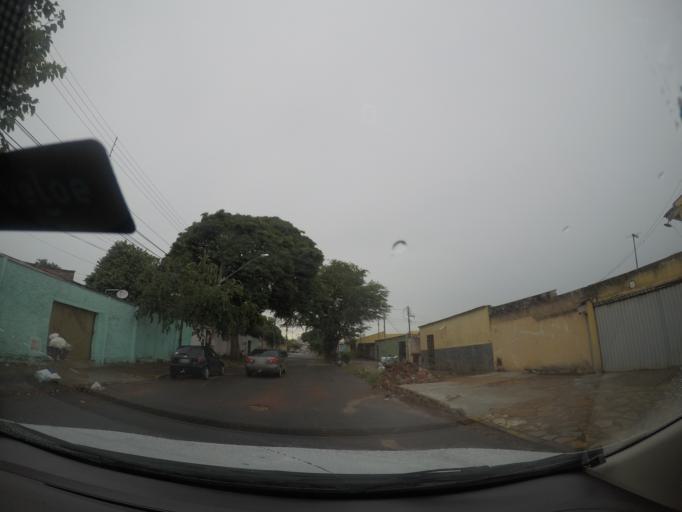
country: BR
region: Goias
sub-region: Goiania
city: Goiania
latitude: -16.6826
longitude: -49.2468
